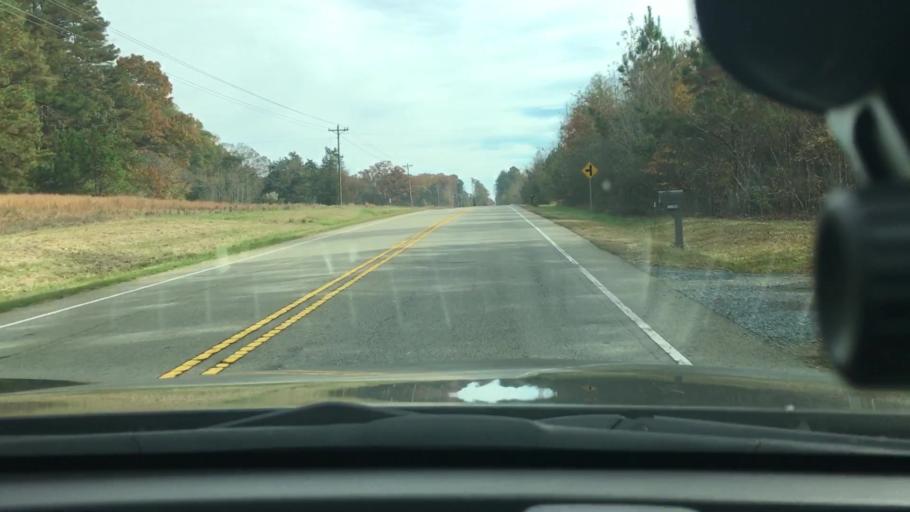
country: US
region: North Carolina
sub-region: Moore County
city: Robbins
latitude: 35.3969
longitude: -79.5345
